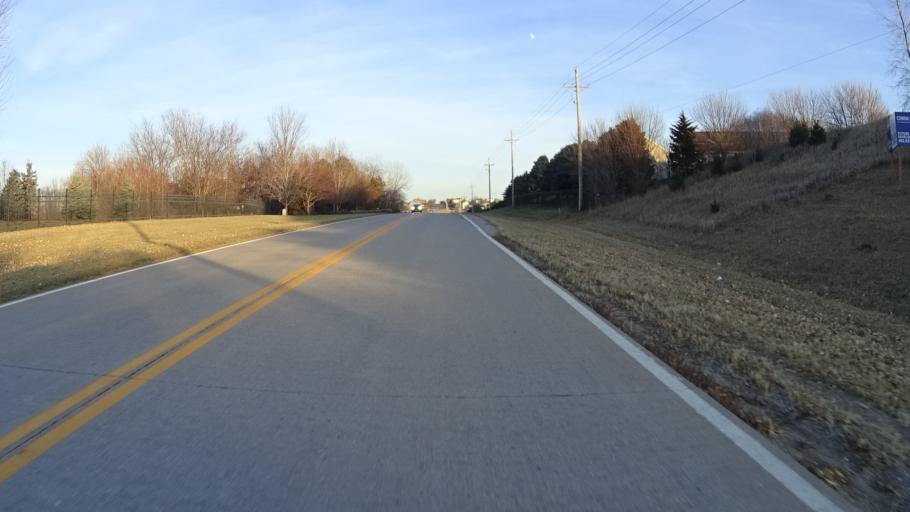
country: US
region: Nebraska
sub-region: Sarpy County
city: Papillion
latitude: 41.1326
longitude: -96.0724
